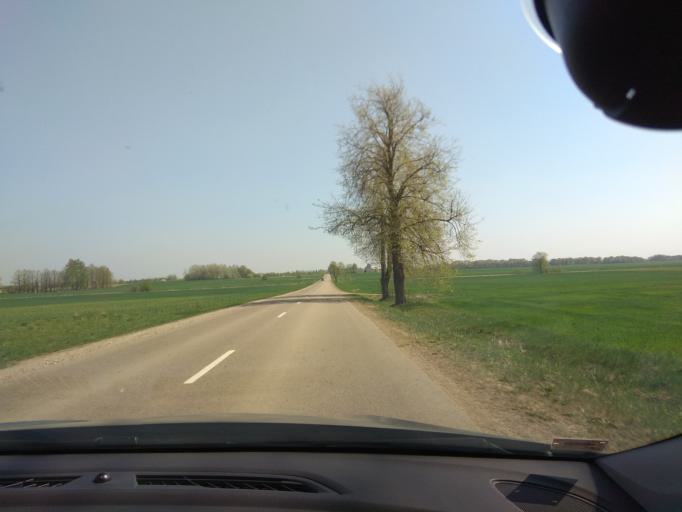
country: LT
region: Panevezys
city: Pasvalys
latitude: 55.9424
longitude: 24.2184
